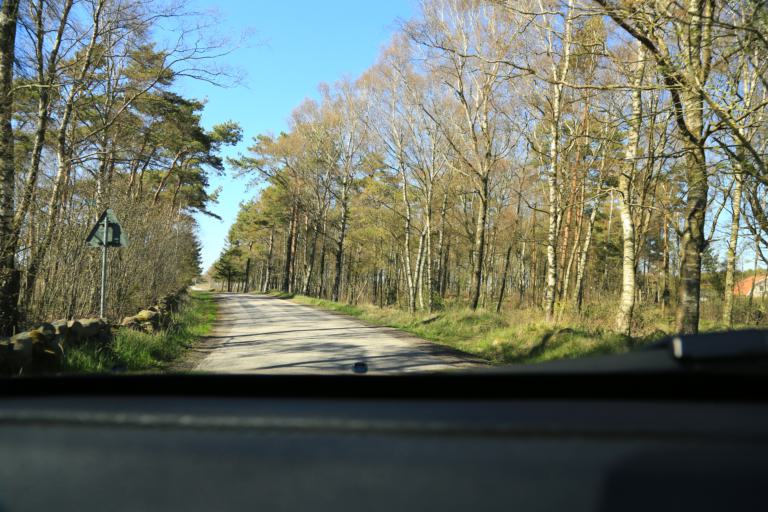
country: SE
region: Halland
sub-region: Varbergs Kommun
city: Traslovslage
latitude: 57.0841
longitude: 12.3107
